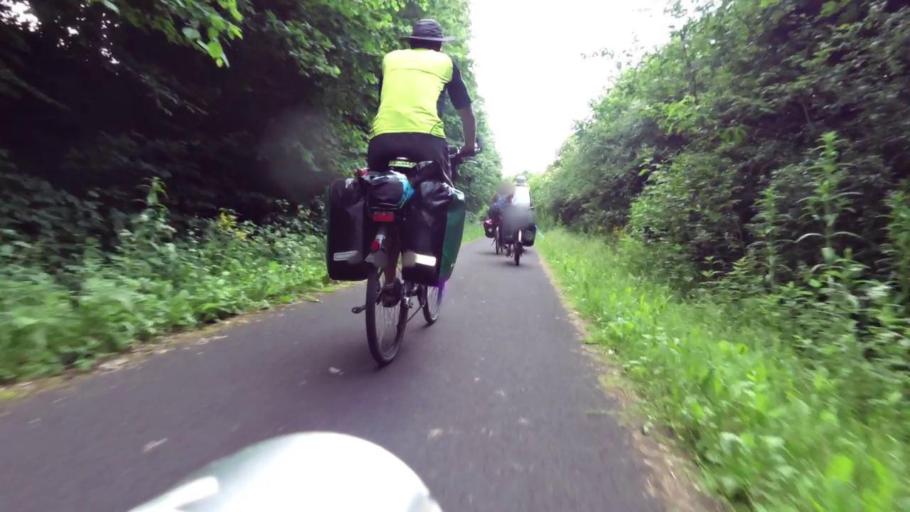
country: PL
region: Kujawsko-Pomorskie
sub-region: Powiat torunski
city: Lubianka
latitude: 53.1116
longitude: 18.5080
